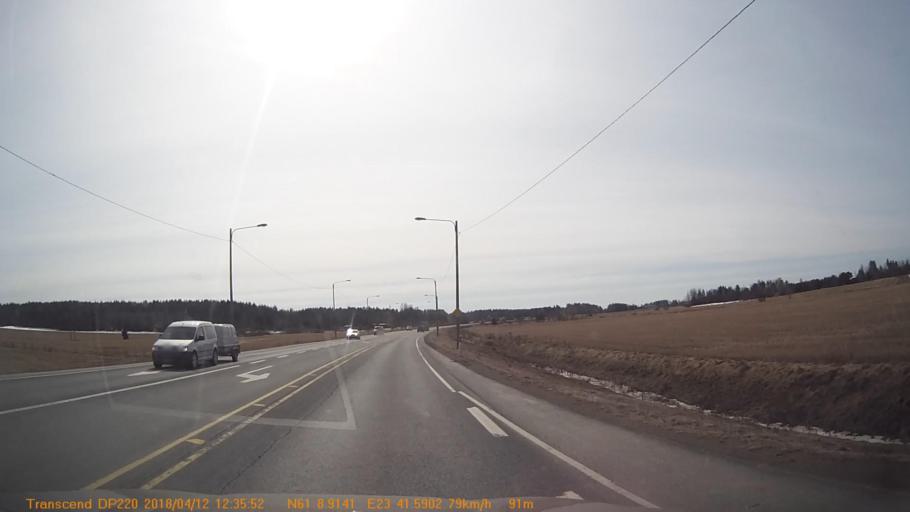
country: FI
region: Pirkanmaa
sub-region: Etelae-Pirkanmaa
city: Kylmaekoski
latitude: 61.1486
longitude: 23.6932
